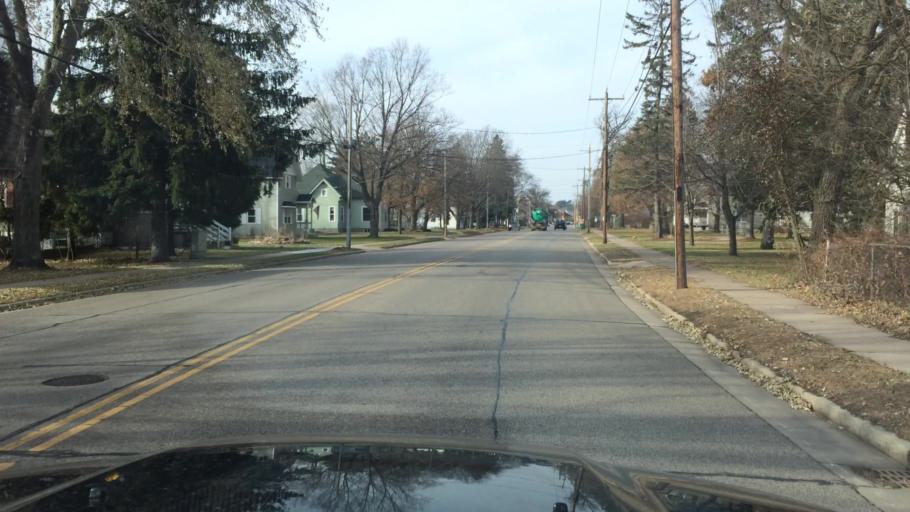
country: US
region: Wisconsin
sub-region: Waupaca County
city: Waupaca
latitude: 44.3530
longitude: -89.0767
